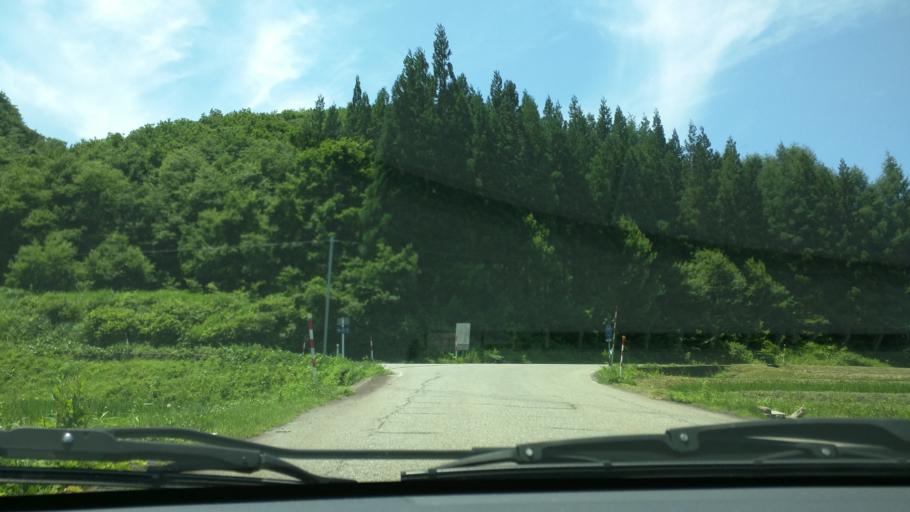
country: JP
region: Tochigi
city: Kuroiso
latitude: 37.2547
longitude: 139.7688
